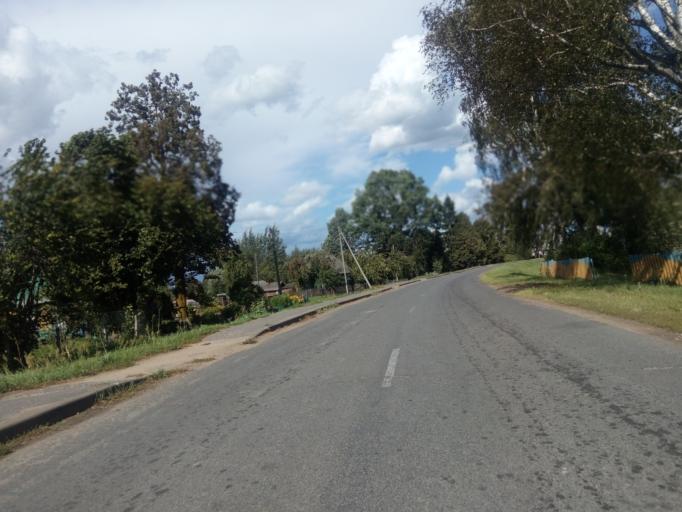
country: BY
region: Vitebsk
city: Dzisna
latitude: 55.7112
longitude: 28.1872
